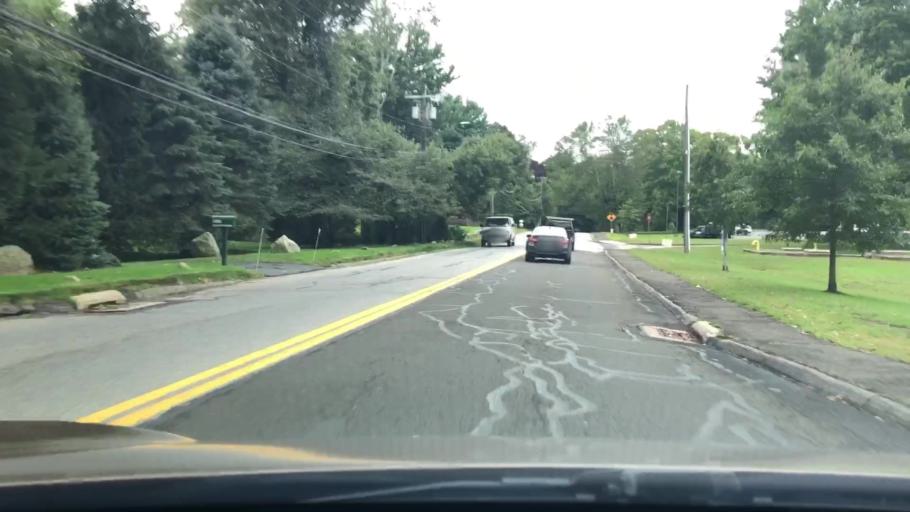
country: US
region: Connecticut
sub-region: Fairfield County
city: Darien
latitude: 41.1158
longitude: -73.4524
